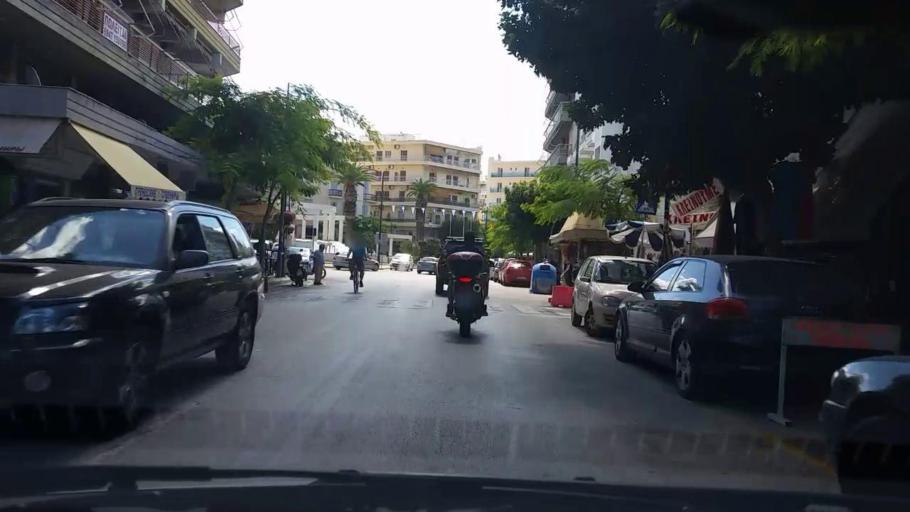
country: GR
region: Peloponnese
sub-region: Nomos Korinthias
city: Loutraki
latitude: 37.9789
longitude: 22.9768
